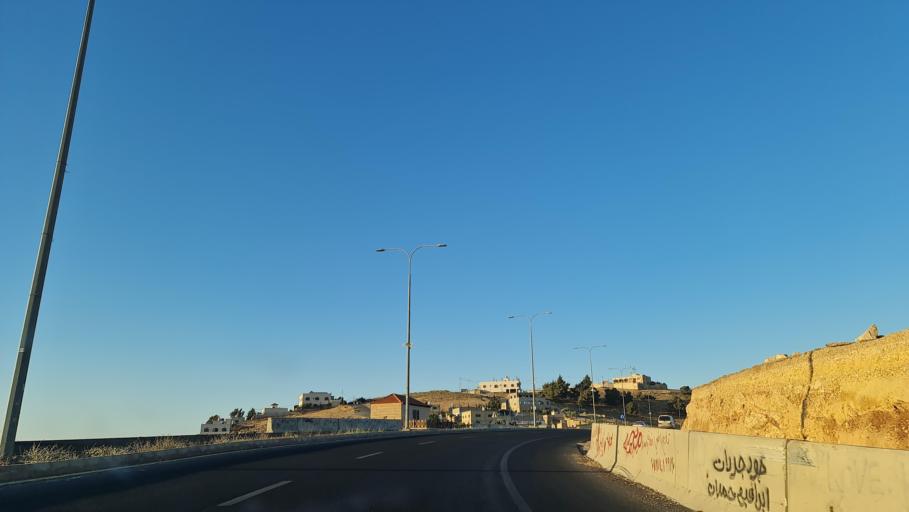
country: JO
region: Zarqa
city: Russeifa
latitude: 32.0917
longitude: 35.9621
